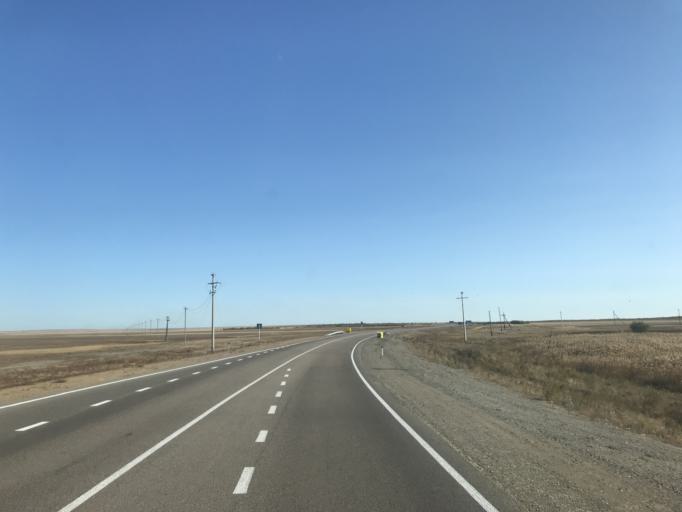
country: KZ
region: Pavlodar
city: Koktobe
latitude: 51.8816
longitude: 77.4205
